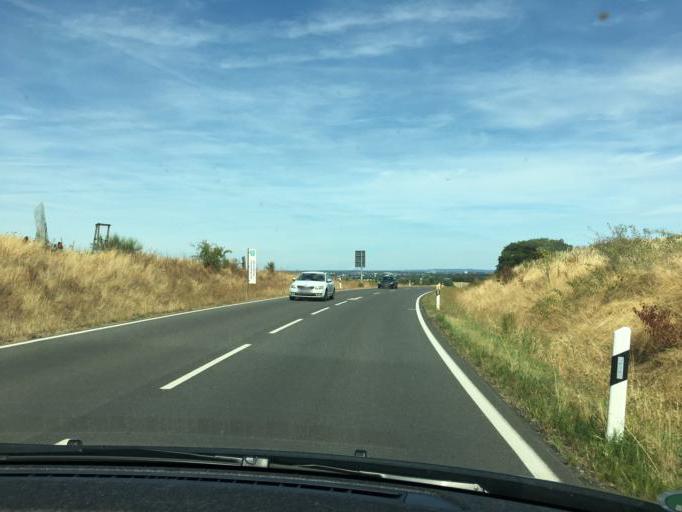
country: DE
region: North Rhine-Westphalia
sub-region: Regierungsbezirk Koln
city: Kreuzau
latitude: 50.7555
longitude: 6.4273
